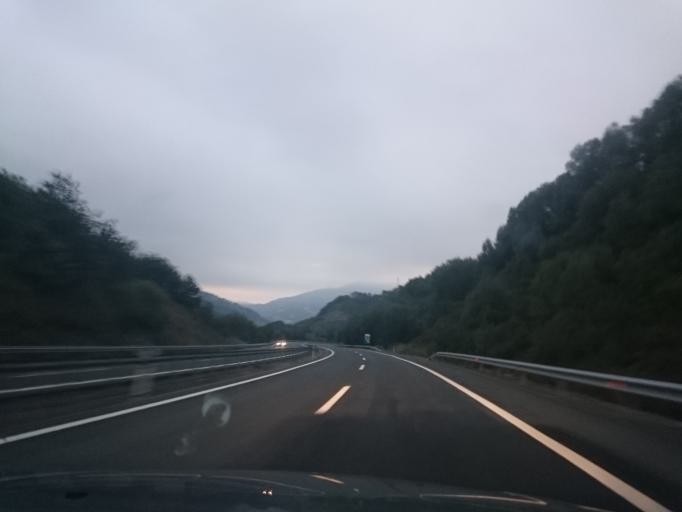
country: ES
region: Asturias
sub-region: Province of Asturias
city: Pola de Lena
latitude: 43.0834
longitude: -5.8251
